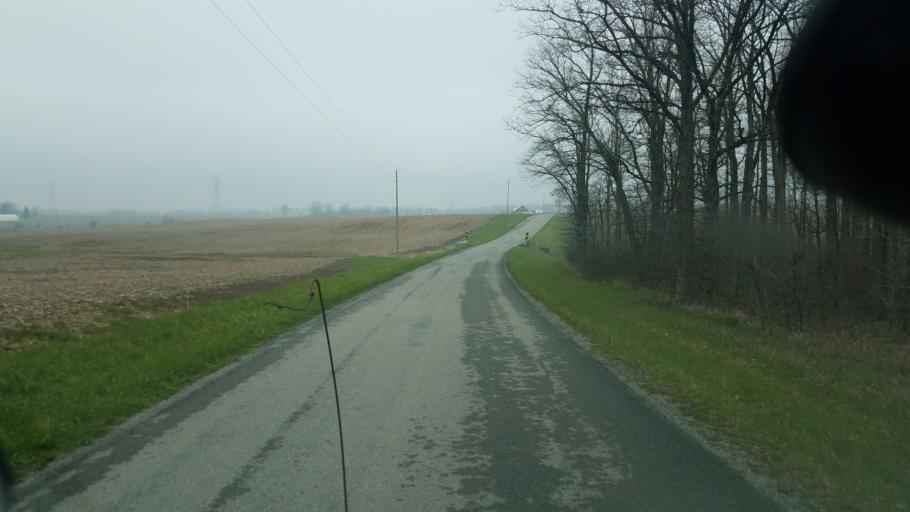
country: US
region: Ohio
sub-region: Logan County
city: Northwood
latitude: 40.5368
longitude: -83.6644
